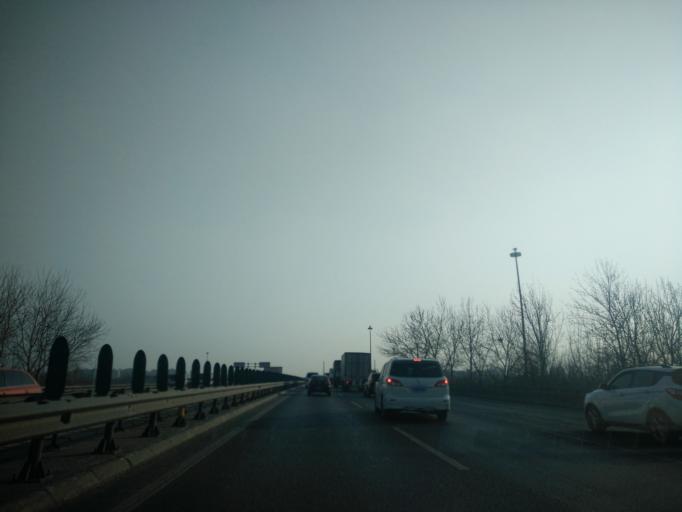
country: CN
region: Beijing
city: Dongfeng
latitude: 39.8706
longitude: 116.5428
